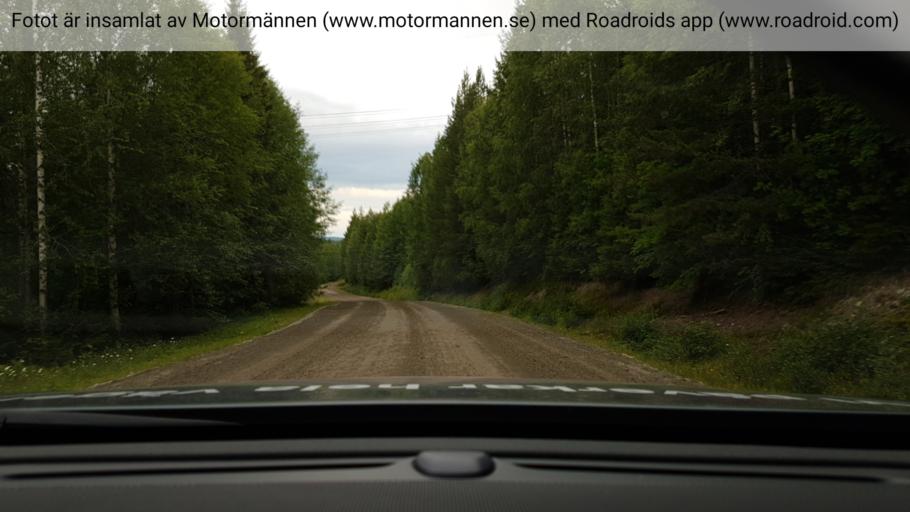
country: SE
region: Vaesterbotten
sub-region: Vannas Kommun
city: Vannasby
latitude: 64.0908
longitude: 20.0323
